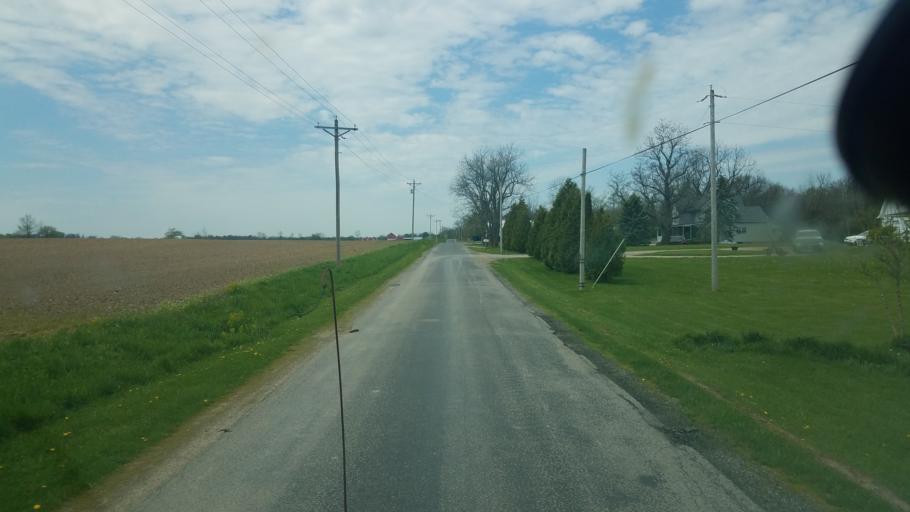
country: US
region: Ohio
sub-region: Hardin County
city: Ada
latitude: 40.7910
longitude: -83.8671
